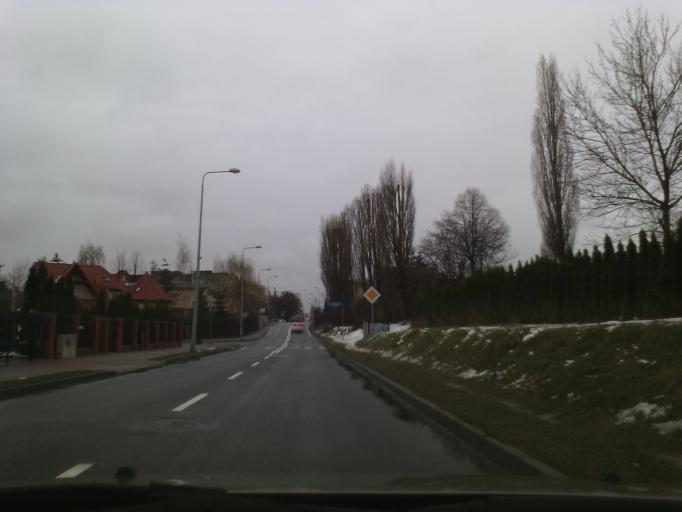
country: PL
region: Lower Silesian Voivodeship
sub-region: Powiat swidnicki
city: Swidnica
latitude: 50.8402
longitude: 16.4698
